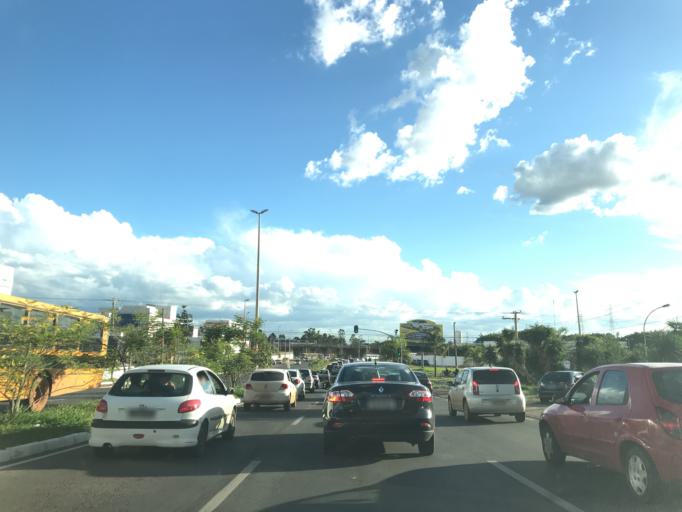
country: BR
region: Federal District
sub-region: Brasilia
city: Brasilia
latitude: -15.8041
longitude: -47.9681
